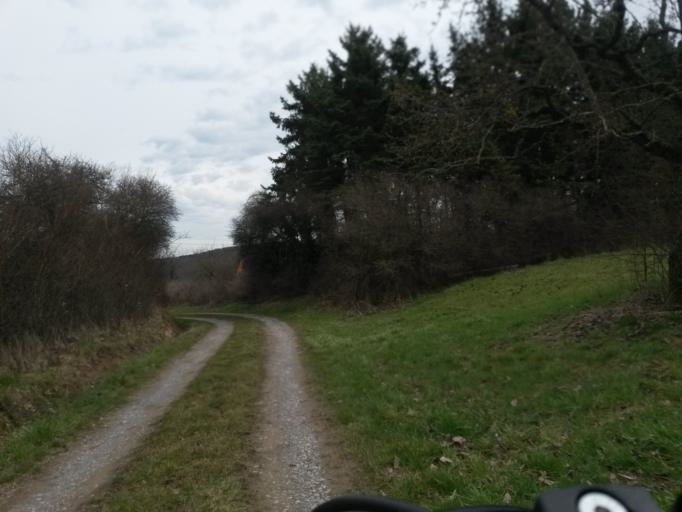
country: DE
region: Baden-Wuerttemberg
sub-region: Karlsruhe Region
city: Konigsbach-Stein
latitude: 48.9145
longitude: 8.5457
